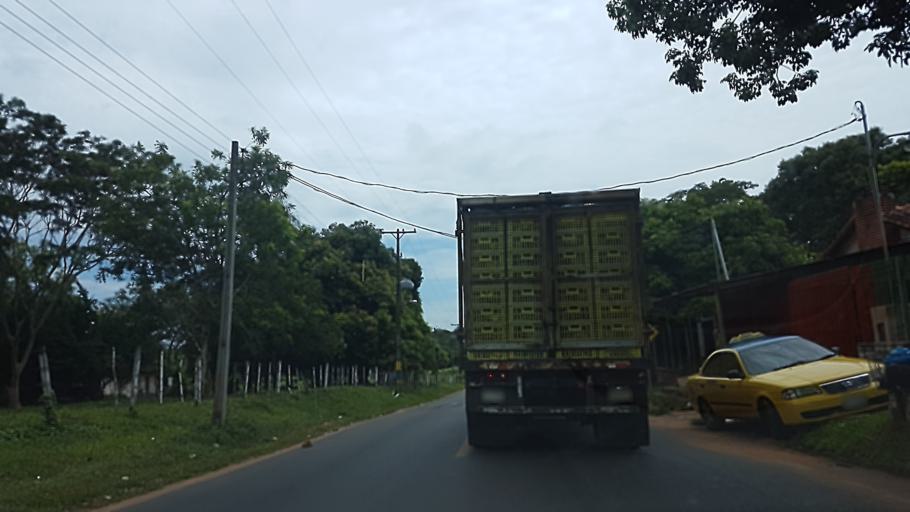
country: PY
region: Central
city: Capiata
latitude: -25.3046
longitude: -57.4656
